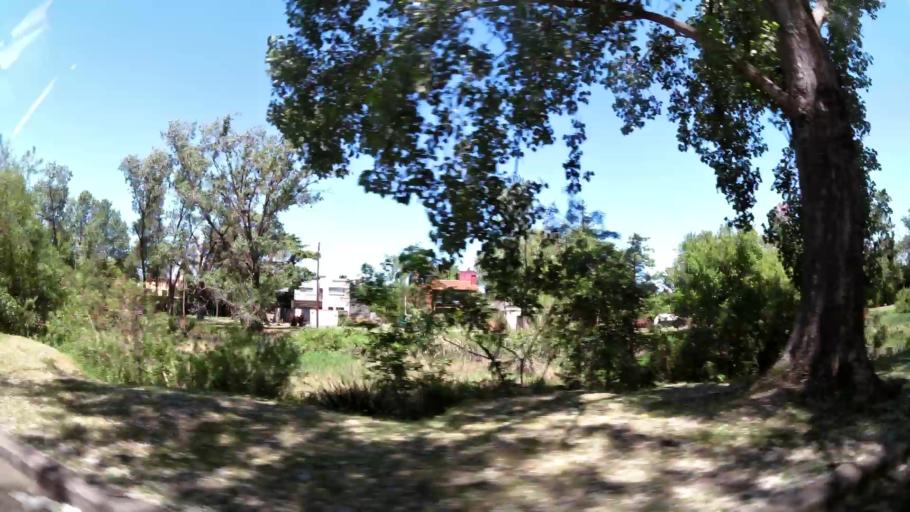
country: AR
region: Buenos Aires
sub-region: Partido de San Isidro
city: San Isidro
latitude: -34.4512
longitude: -58.5196
